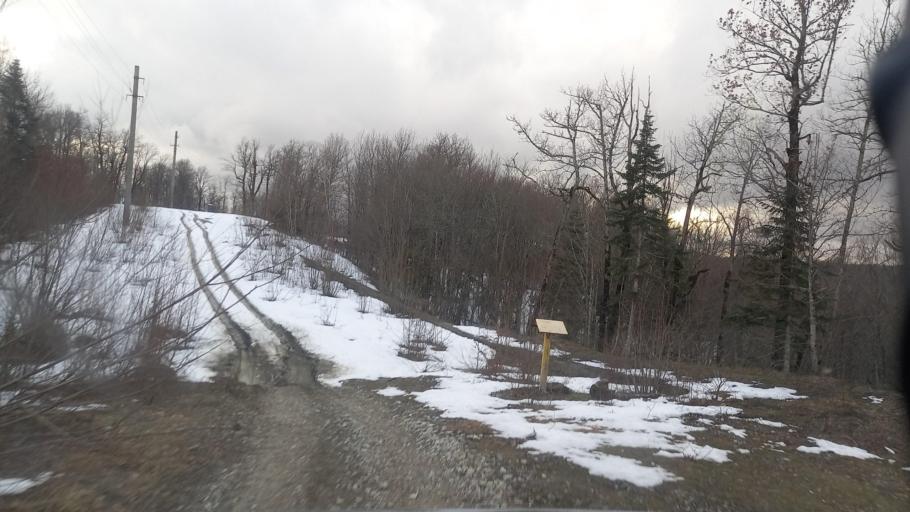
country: RU
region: Krasnodarskiy
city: Dzhubga
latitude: 44.5056
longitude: 38.7690
